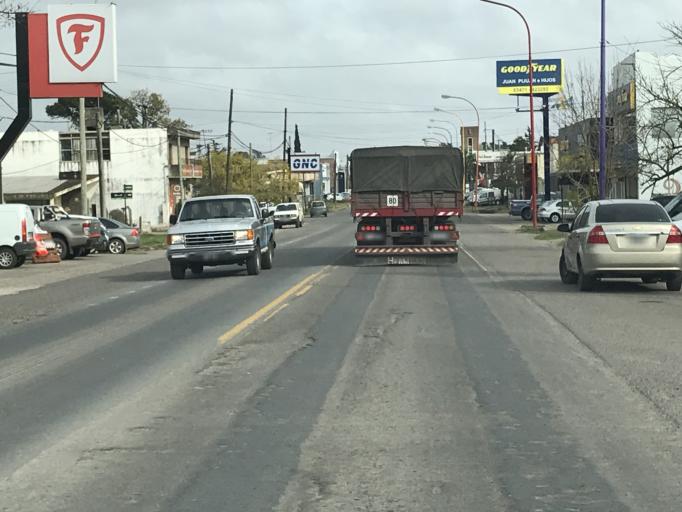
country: AR
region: Santa Fe
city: Canada de Gomez
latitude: -32.8112
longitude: -61.3895
